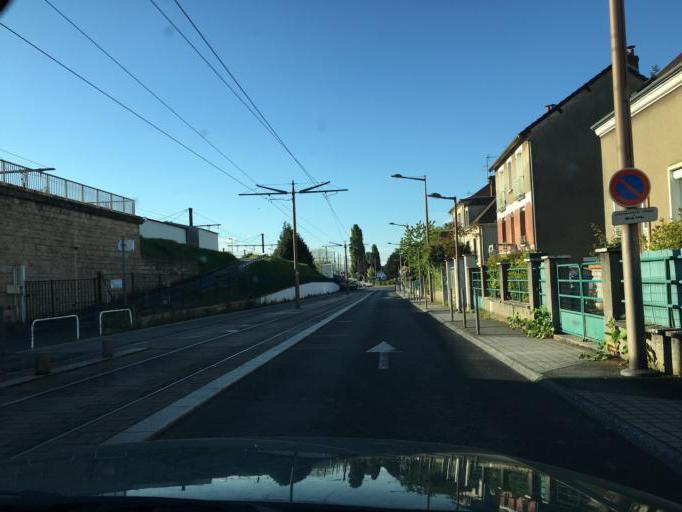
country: FR
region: Centre
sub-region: Departement du Loiret
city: Fleury-les-Aubrais
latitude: 47.9275
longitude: 1.9066
